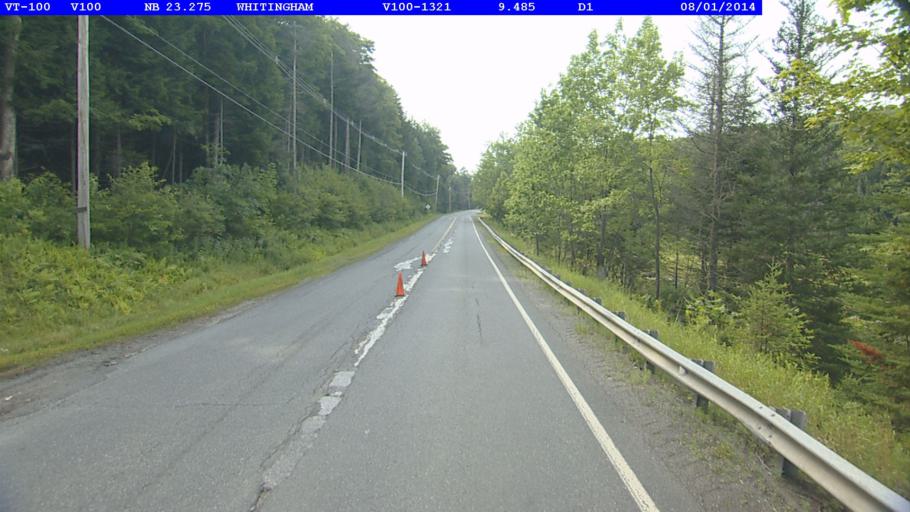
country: US
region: Vermont
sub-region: Windham County
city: Dover
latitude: 42.8146
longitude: -72.8464
